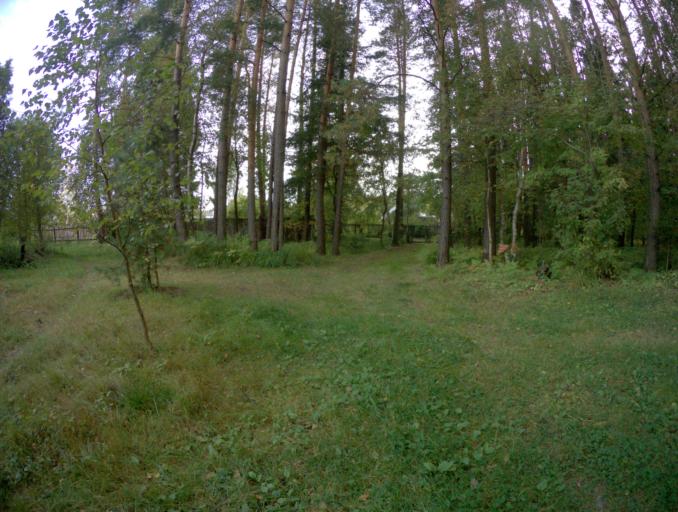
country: RU
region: Vladimir
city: Raduzhnyy
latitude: 56.0585
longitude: 40.3633
